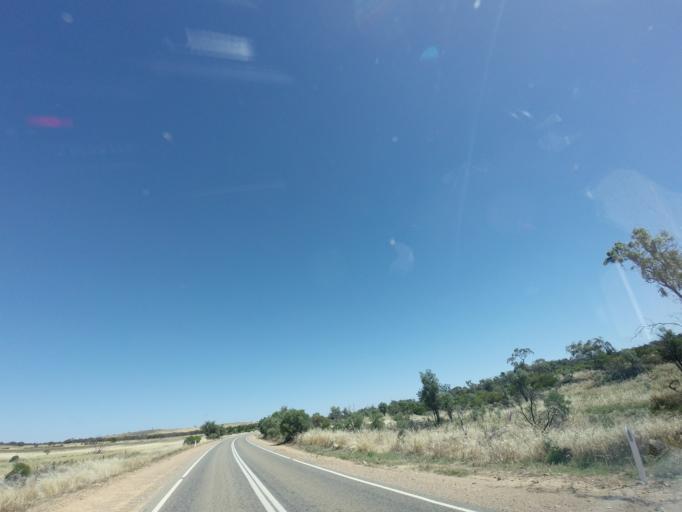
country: AU
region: South Australia
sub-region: Peterborough
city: Peterborough
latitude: -32.9156
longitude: 138.7680
